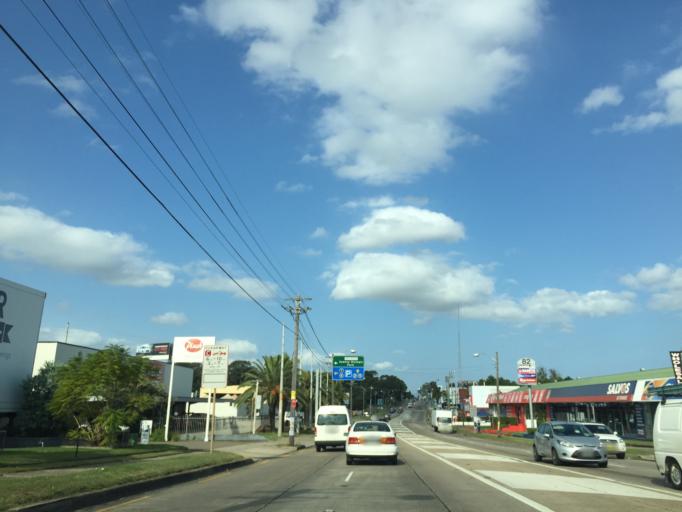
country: AU
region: New South Wales
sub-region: Auburn
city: Auburn
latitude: -33.8493
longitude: 151.0507
